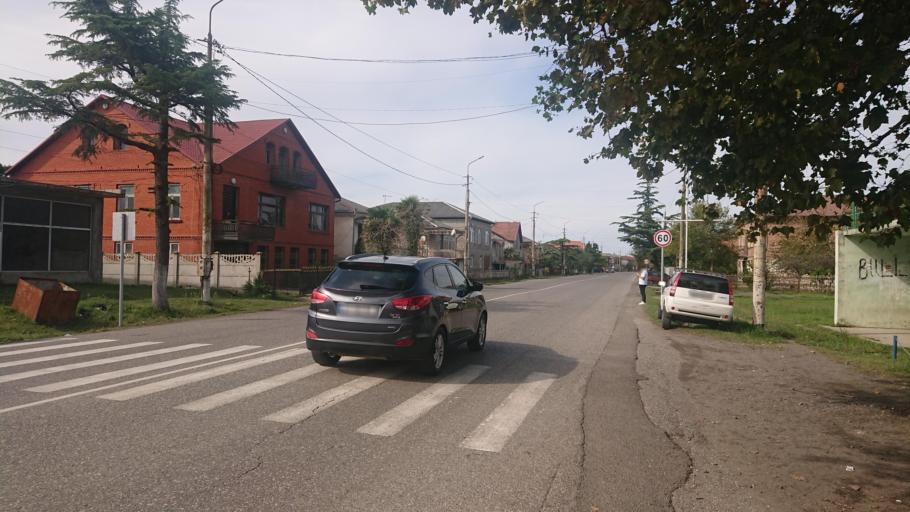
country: GE
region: Samegrelo and Zemo Svaneti
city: P'ot'i
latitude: 42.1254
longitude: 41.6911
